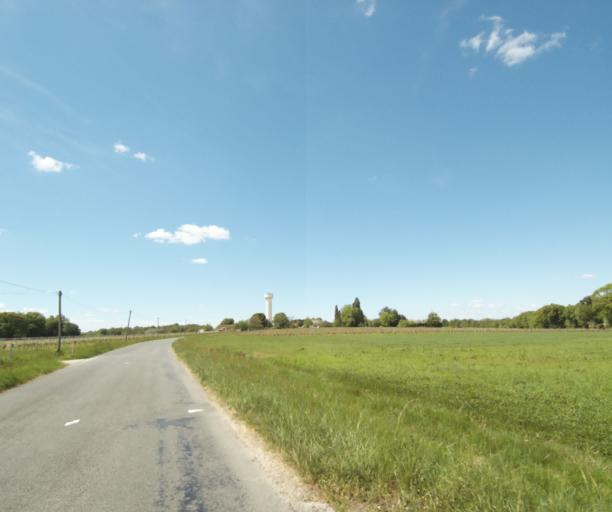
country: FR
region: Poitou-Charentes
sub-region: Departement de la Charente-Maritime
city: Burie
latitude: 45.7604
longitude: -0.4706
